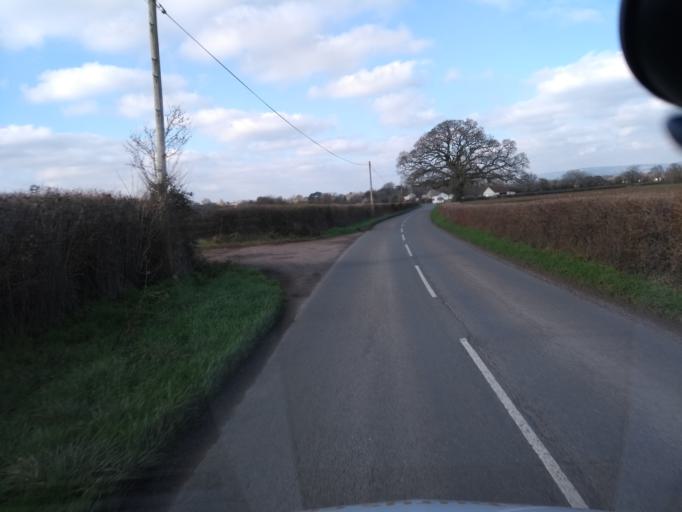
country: GB
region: England
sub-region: Somerset
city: Creech Saint Michael
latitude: 50.9855
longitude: -3.0654
